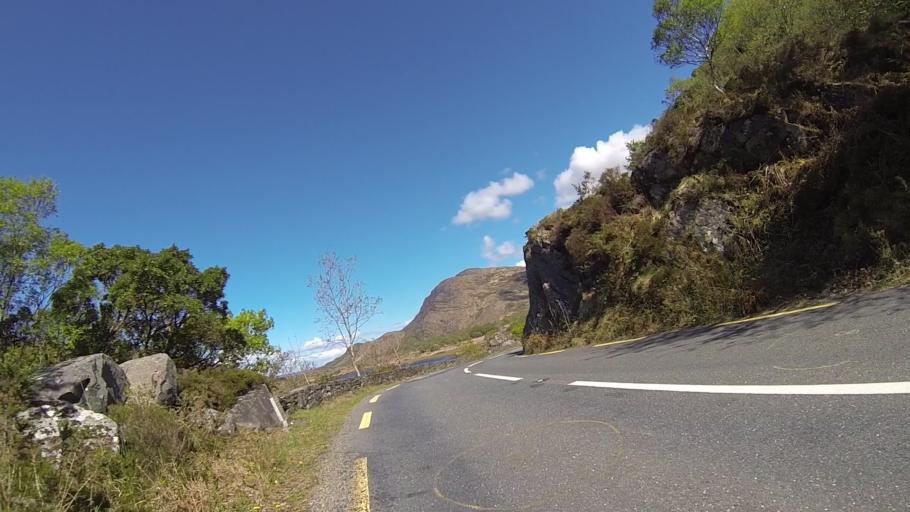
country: IE
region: Munster
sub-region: Ciarrai
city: Cill Airne
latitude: 51.9842
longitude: -9.5682
